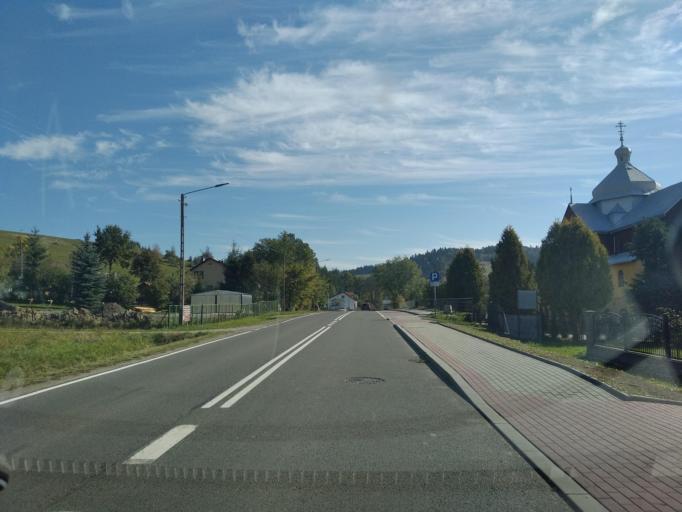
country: PL
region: Subcarpathian Voivodeship
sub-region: Powiat sanocki
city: Komancza
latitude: 49.3393
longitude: 22.0619
